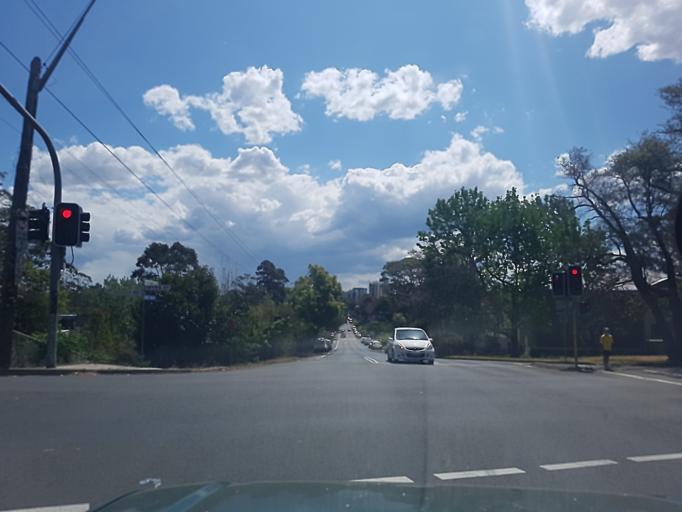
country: AU
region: New South Wales
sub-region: Hornsby Shire
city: Hornsby
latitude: -33.7126
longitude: 151.1097
